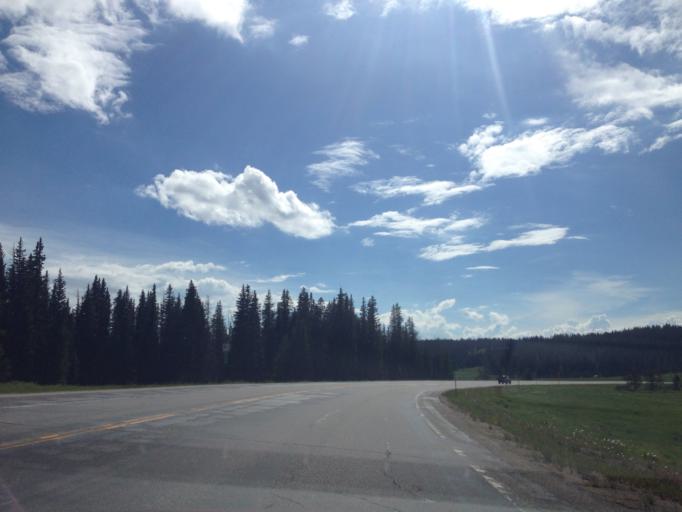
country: US
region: Colorado
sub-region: Routt County
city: Steamboat Springs
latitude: 40.3839
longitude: -106.6124
